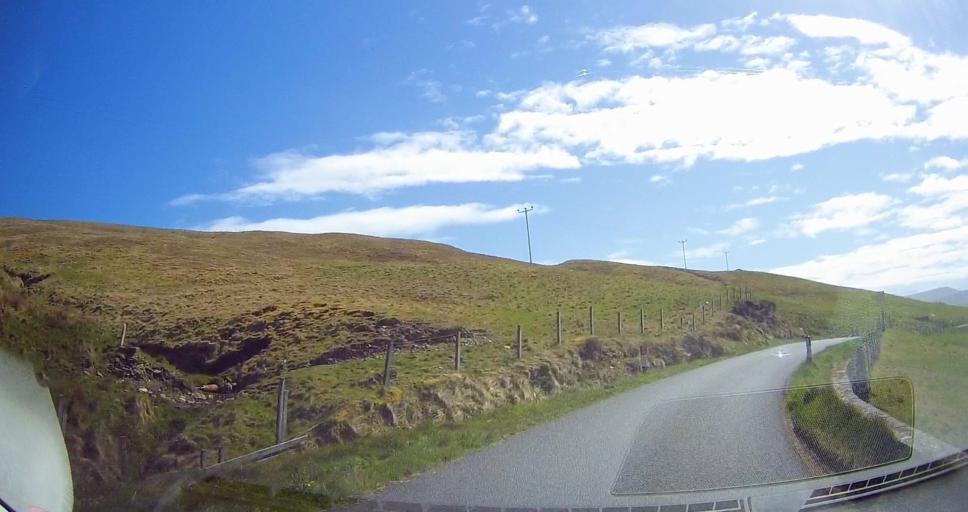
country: GB
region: Scotland
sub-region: Shetland Islands
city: Sandwick
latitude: 59.9559
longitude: -1.3259
